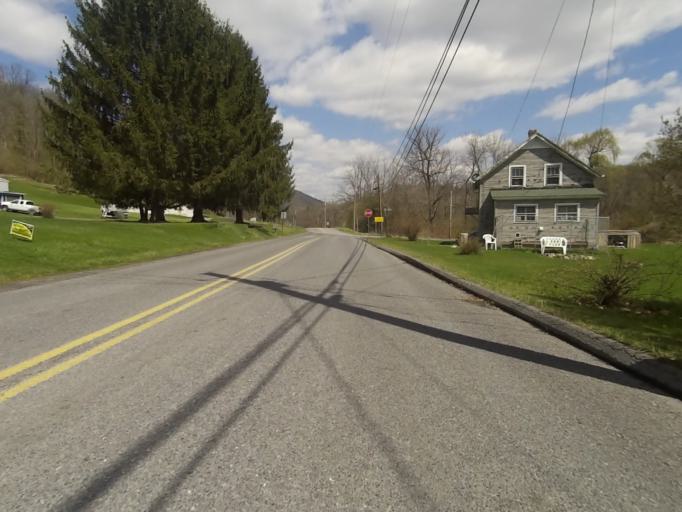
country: US
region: Pennsylvania
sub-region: Centre County
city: Bellefonte
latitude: 40.8961
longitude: -77.7978
